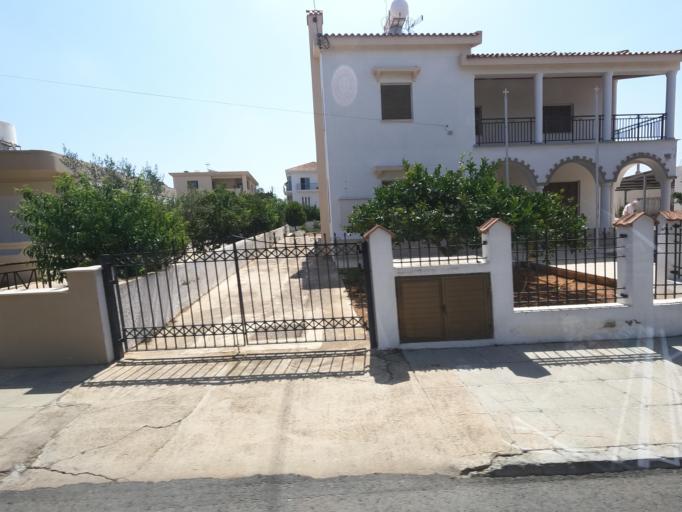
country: CY
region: Ammochostos
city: Paralimni
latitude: 35.0450
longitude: 33.9819
